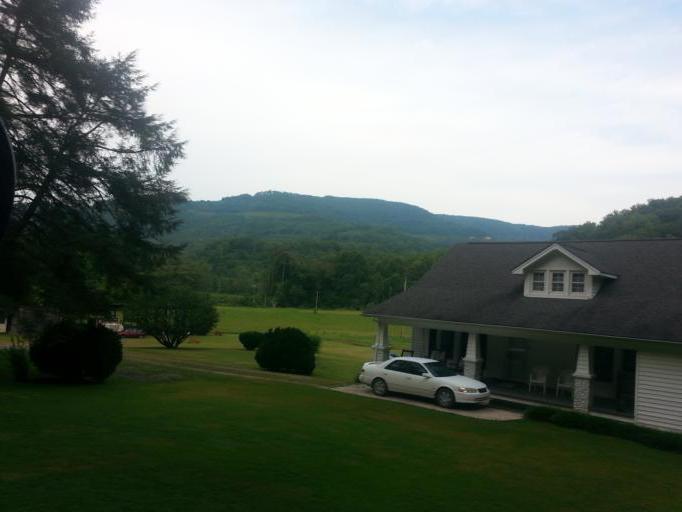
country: US
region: Tennessee
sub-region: Roane County
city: Oliver Springs
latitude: 36.1688
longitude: -84.3546
